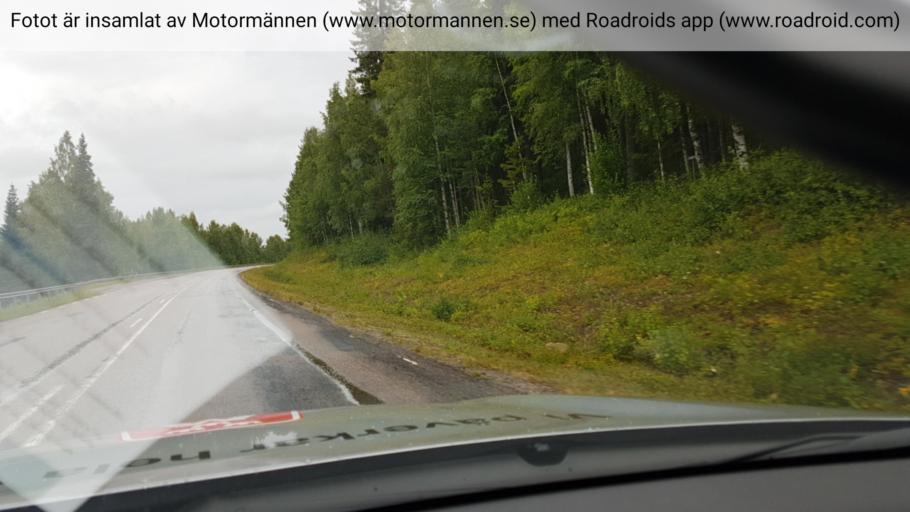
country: SE
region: Norrbotten
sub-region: Alvsbyns Kommun
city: AElvsbyn
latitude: 66.1455
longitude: 20.8762
